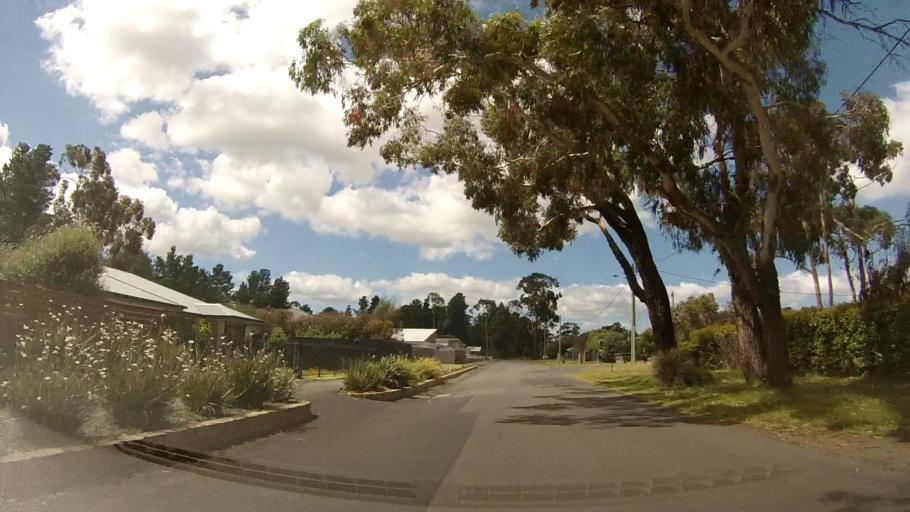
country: AU
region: Tasmania
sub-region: Clarence
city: Seven Mile Beach
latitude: -42.8564
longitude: 147.5040
